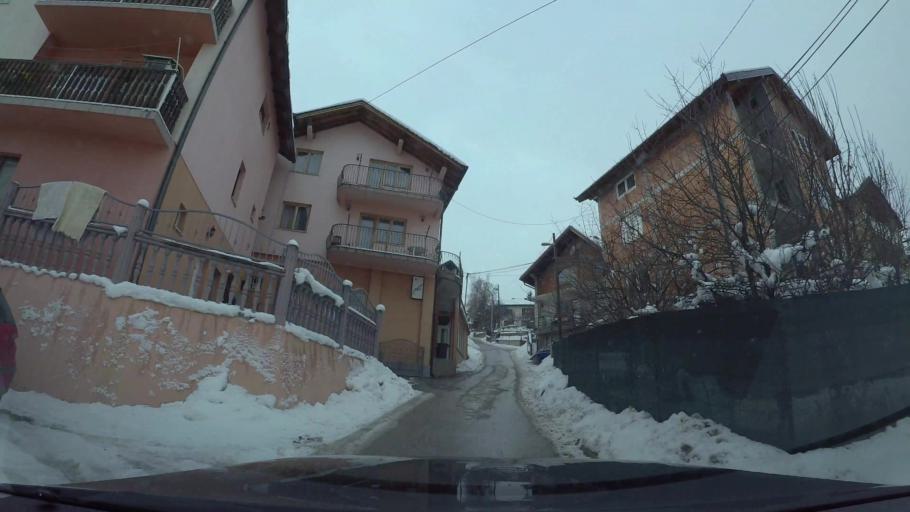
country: BA
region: Federation of Bosnia and Herzegovina
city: Kobilja Glava
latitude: 43.8701
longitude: 18.3977
